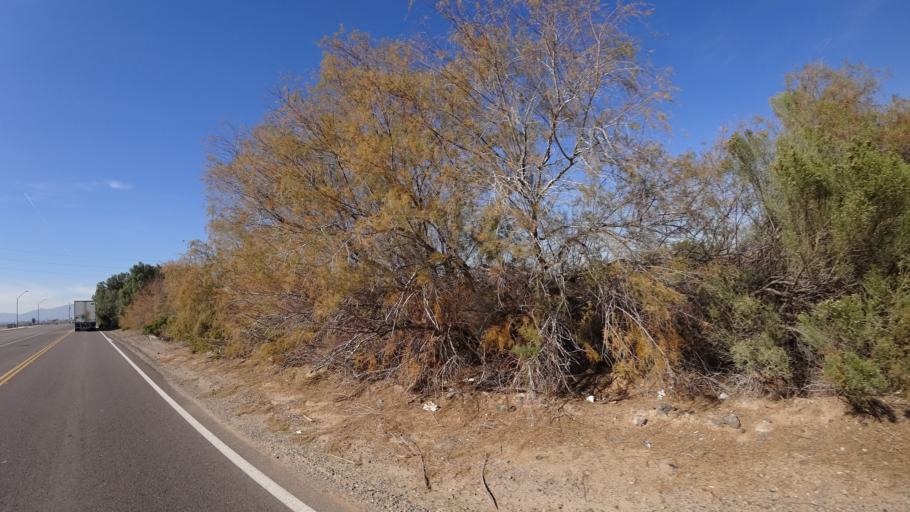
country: US
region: Arizona
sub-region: Maricopa County
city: Citrus Park
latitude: 33.5082
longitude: -112.4238
